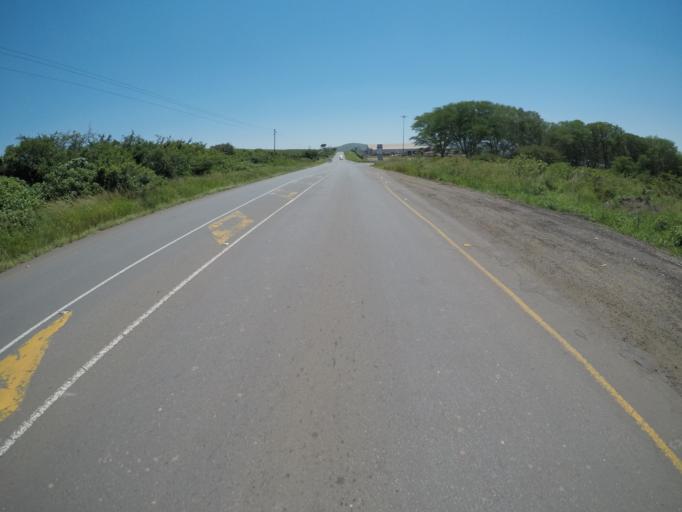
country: ZA
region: KwaZulu-Natal
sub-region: uThungulu District Municipality
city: Empangeni
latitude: -28.7294
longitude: 31.8712
